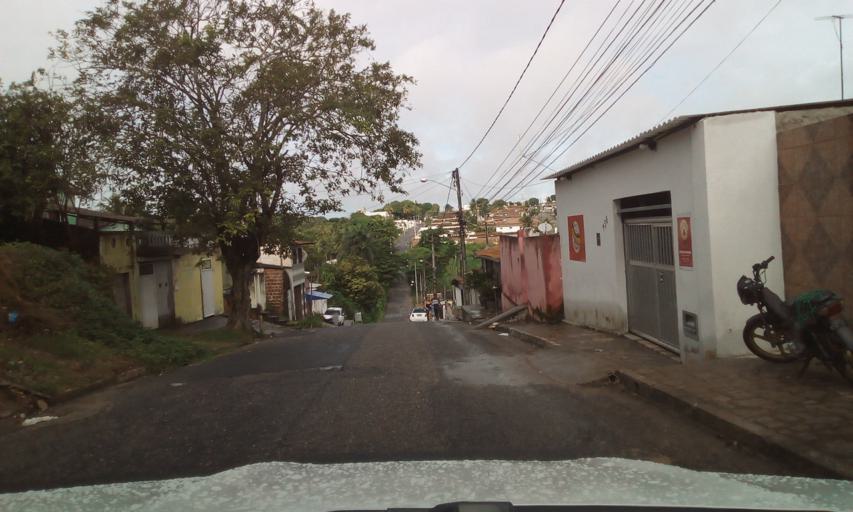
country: BR
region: Paraiba
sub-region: Joao Pessoa
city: Joao Pessoa
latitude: -7.1446
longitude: -34.8839
